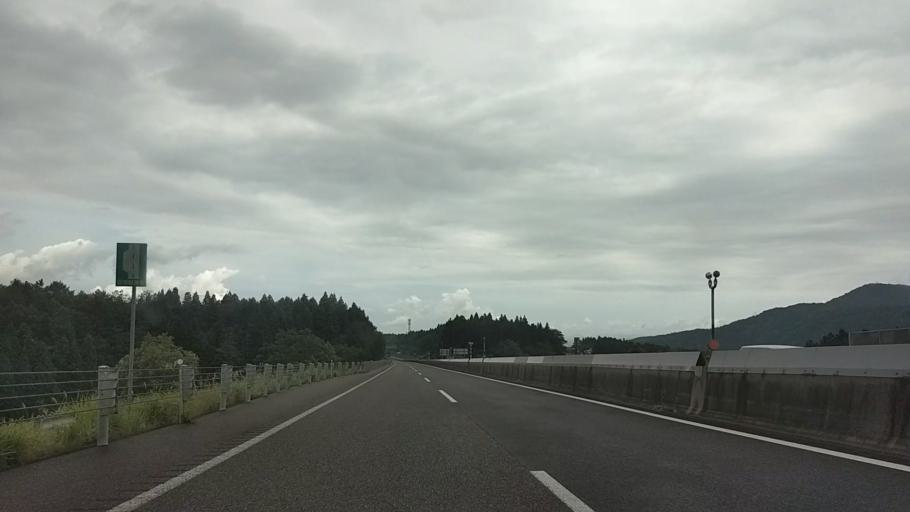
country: JP
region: Niigata
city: Arai
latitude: 36.9539
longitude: 138.2178
